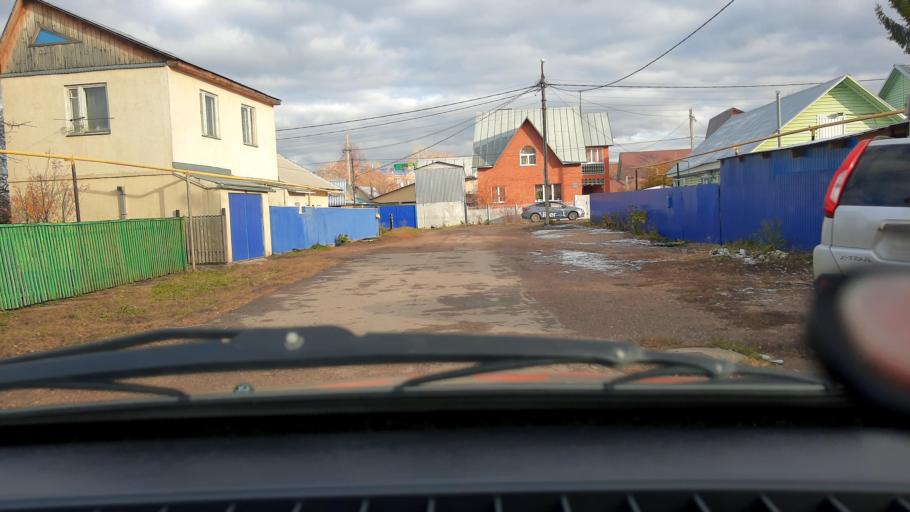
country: RU
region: Bashkortostan
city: Ufa
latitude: 54.7791
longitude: 56.0635
